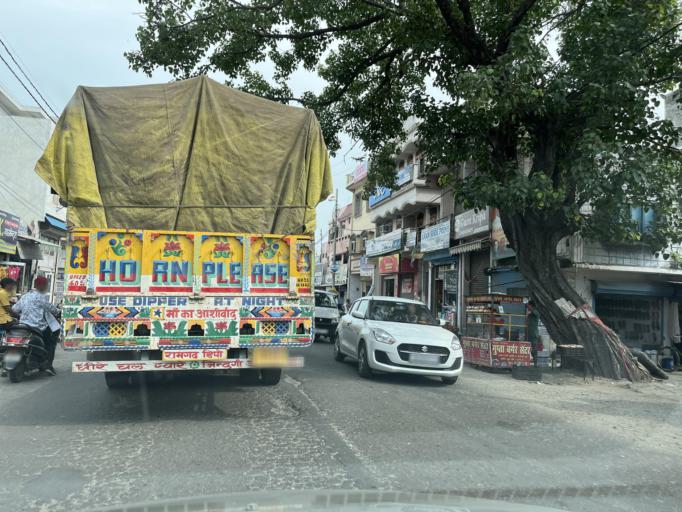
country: IN
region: Uttar Pradesh
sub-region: Rampur
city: Bilaspur
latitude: 29.0430
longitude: 79.2473
